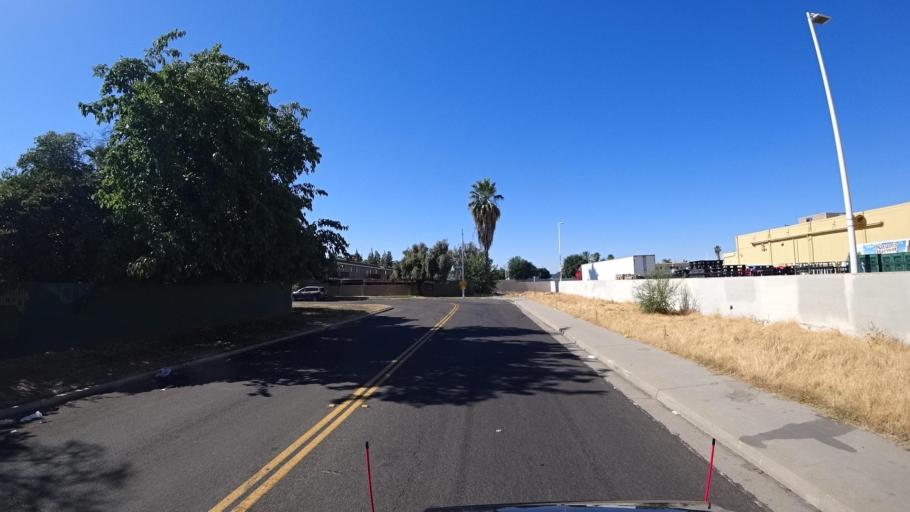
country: US
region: California
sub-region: Fresno County
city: Fresno
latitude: 36.7926
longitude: -119.7883
